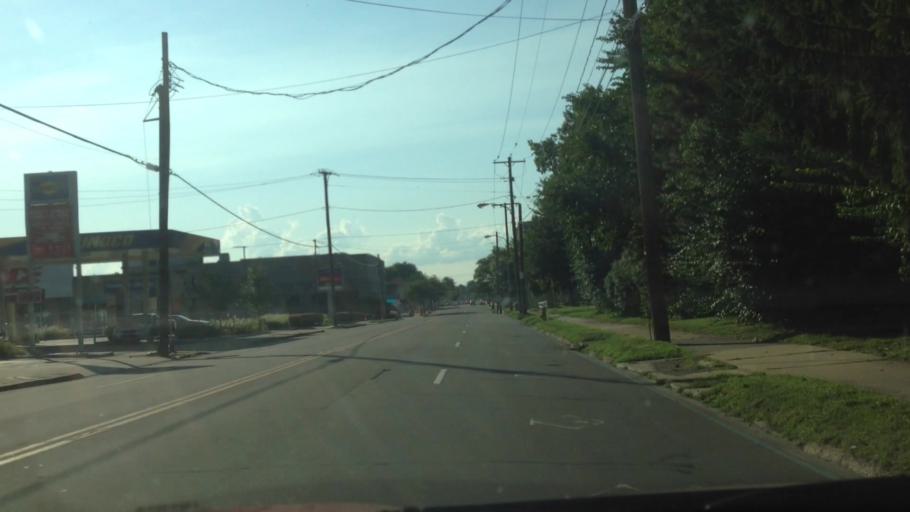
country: US
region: Ohio
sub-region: Summit County
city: Fairlawn
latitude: 41.1078
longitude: -81.5654
